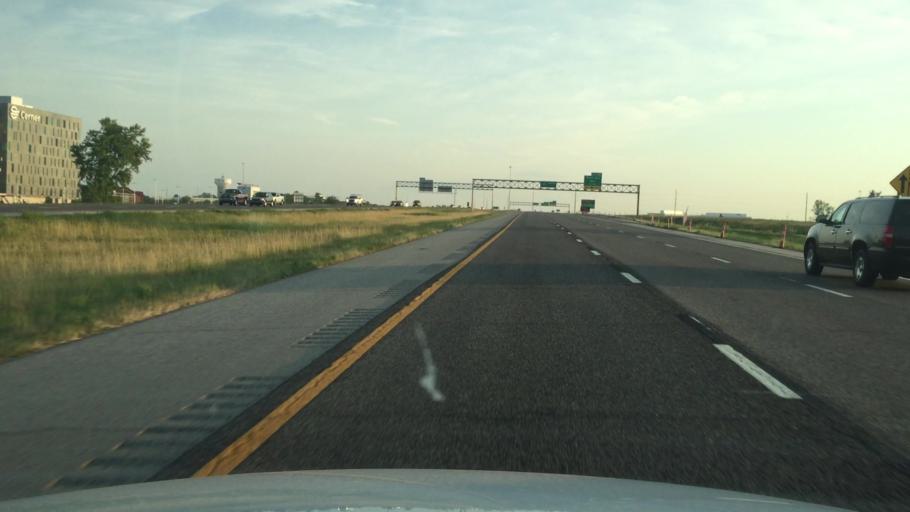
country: US
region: Kansas
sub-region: Wyandotte County
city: Edwardsville
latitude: 39.1113
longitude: -94.8115
